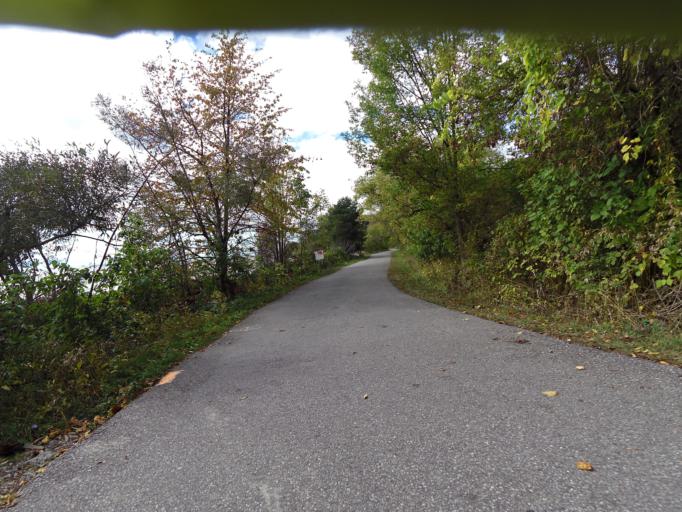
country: CA
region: Ontario
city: Scarborough
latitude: 43.7664
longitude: -79.1458
